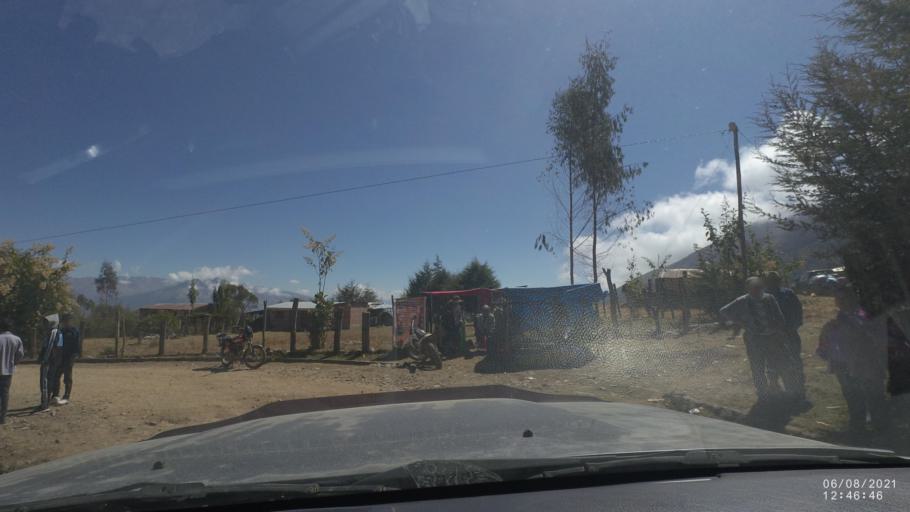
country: BO
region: Cochabamba
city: Colchani
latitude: -16.7622
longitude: -66.6669
